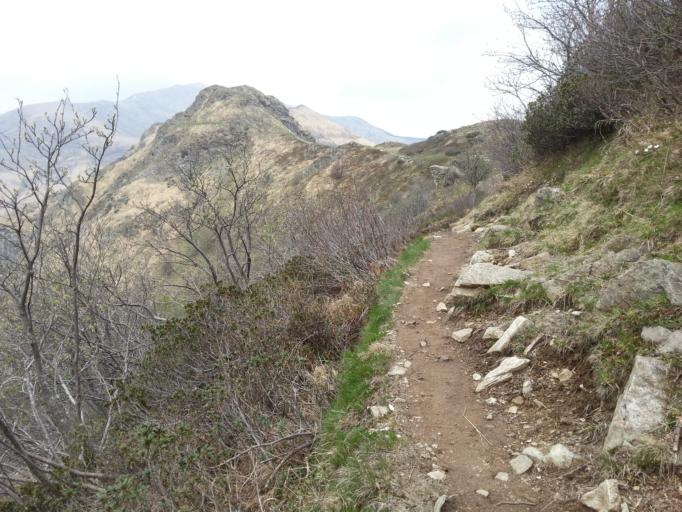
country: IT
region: Lombardy
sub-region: Provincia di Varese
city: Curiglia
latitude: 46.0545
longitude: 8.8541
